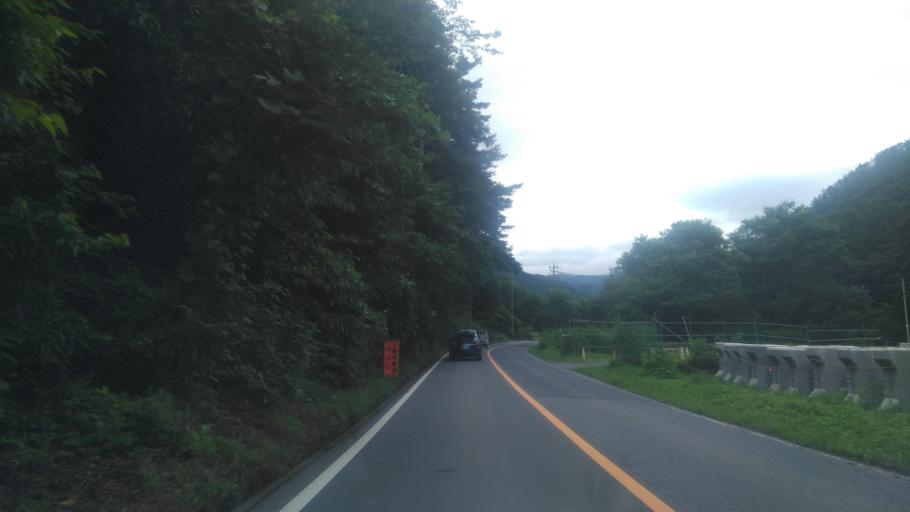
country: JP
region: Nagano
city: Ueda
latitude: 36.4662
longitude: 138.3410
